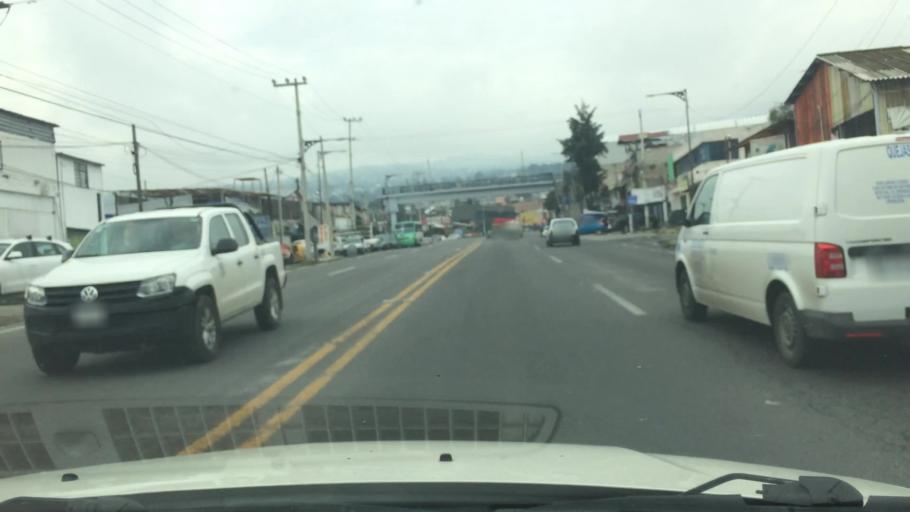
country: MX
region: Mexico City
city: Tlalpan
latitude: 19.2599
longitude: -99.1736
